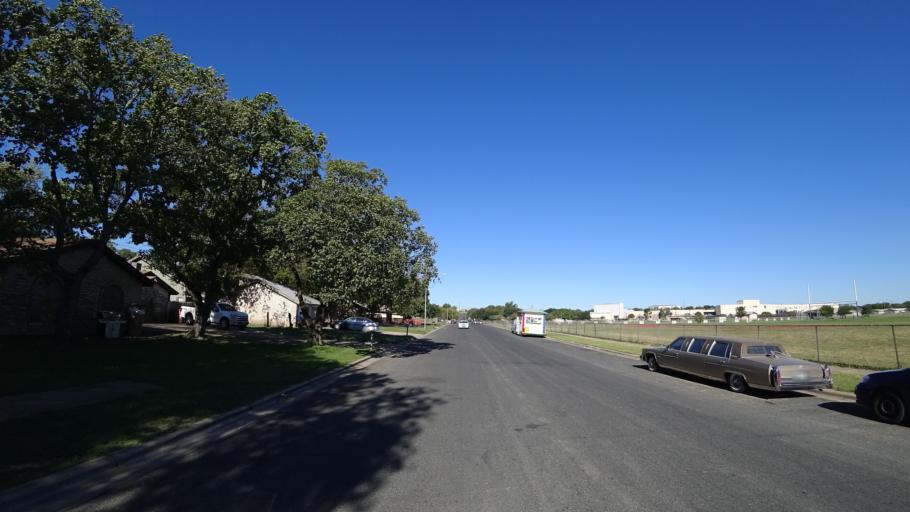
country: US
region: Texas
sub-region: Travis County
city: Hornsby Bend
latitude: 30.3096
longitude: -97.6552
